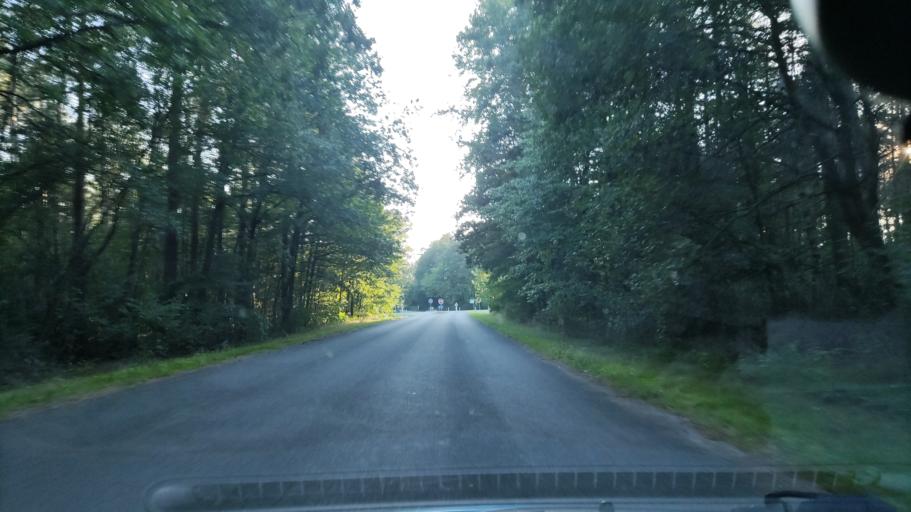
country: DE
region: Lower Saxony
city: Munster
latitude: 52.9744
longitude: 10.1481
